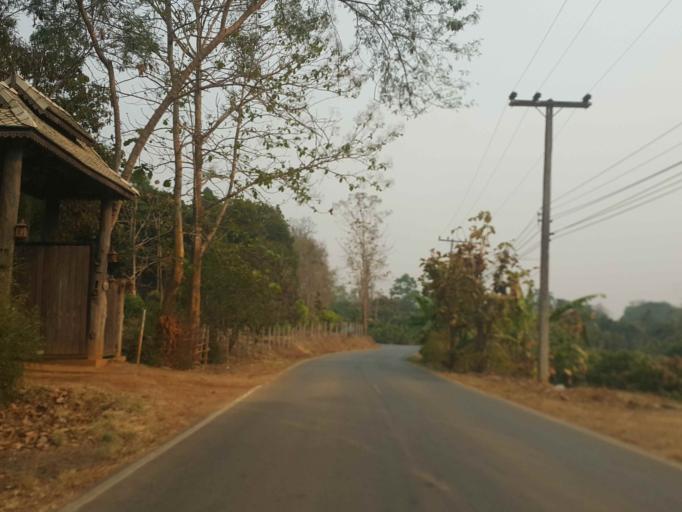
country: TH
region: Chiang Mai
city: Mae Taeng
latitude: 19.1122
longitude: 98.8958
